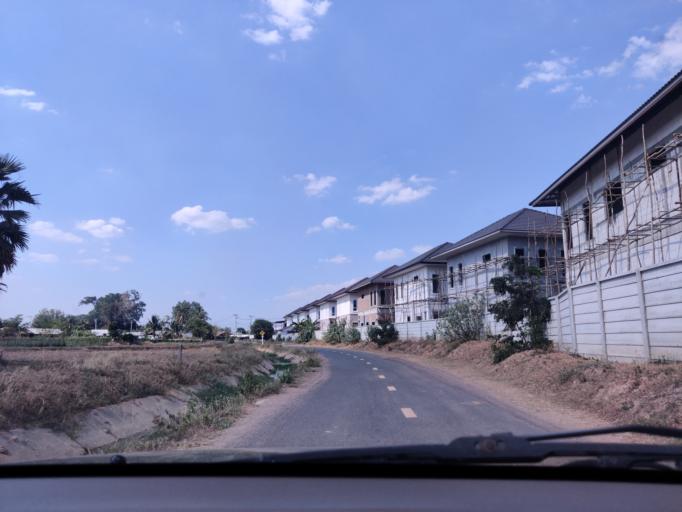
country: TH
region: Sisaket
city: Si Sa Ket
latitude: 15.1007
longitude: 104.3568
